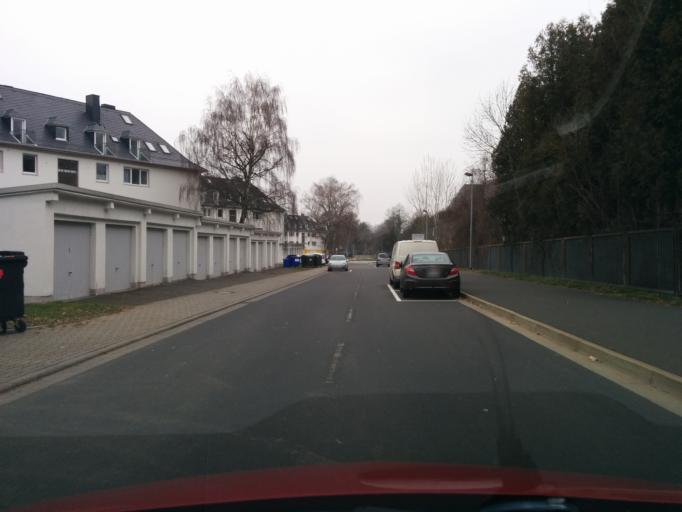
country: DE
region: Rheinland-Pfalz
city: Urbar
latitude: 50.3730
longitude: 7.6339
